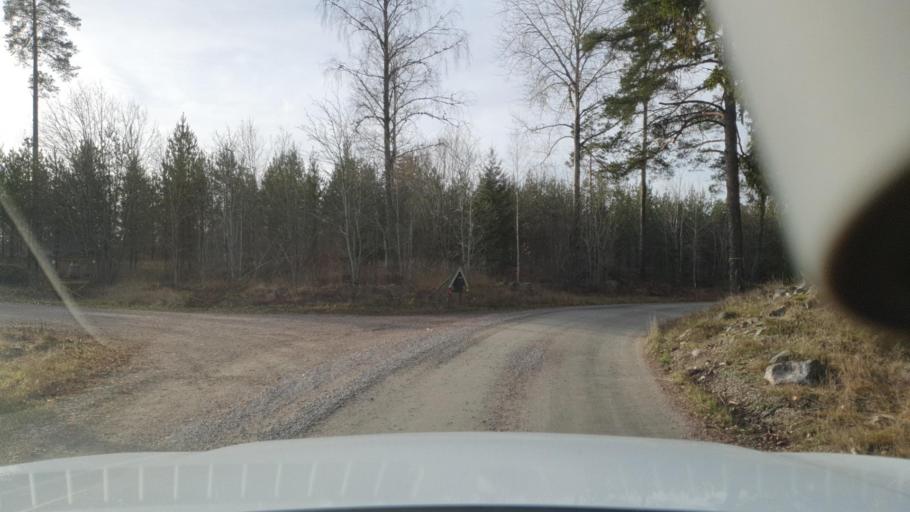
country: SE
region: Uppsala
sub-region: Tierps Kommun
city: Tierp
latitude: 60.3365
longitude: 17.6355
